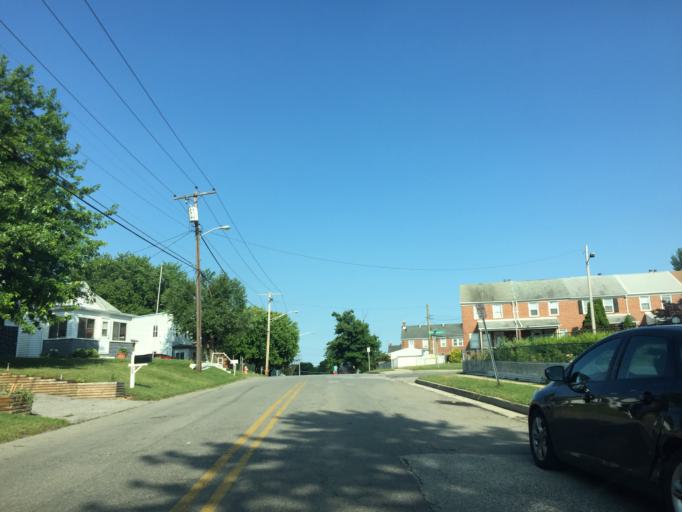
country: US
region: Maryland
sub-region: Baltimore County
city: Rosedale
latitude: 39.2938
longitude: -76.5221
